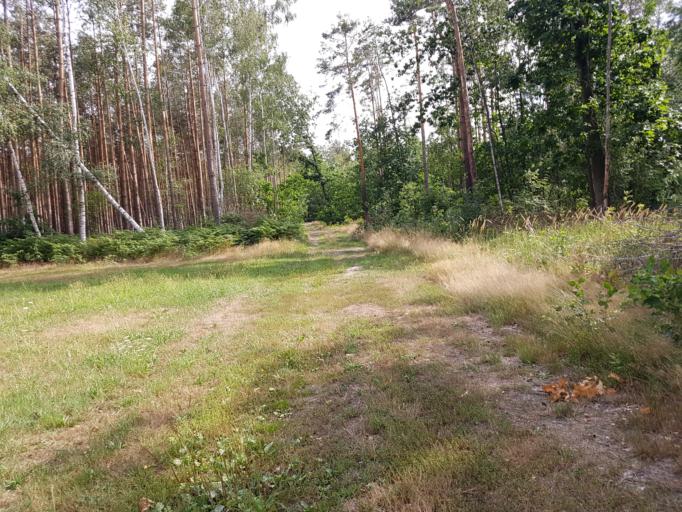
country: DE
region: Brandenburg
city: Doberlug-Kirchhain
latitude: 51.6313
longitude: 13.5970
